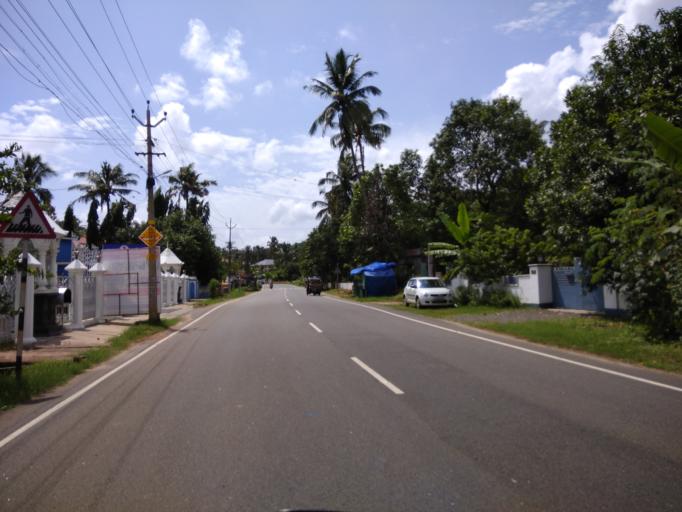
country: IN
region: Kerala
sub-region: Thrissur District
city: Trichur
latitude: 10.5384
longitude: 76.3330
